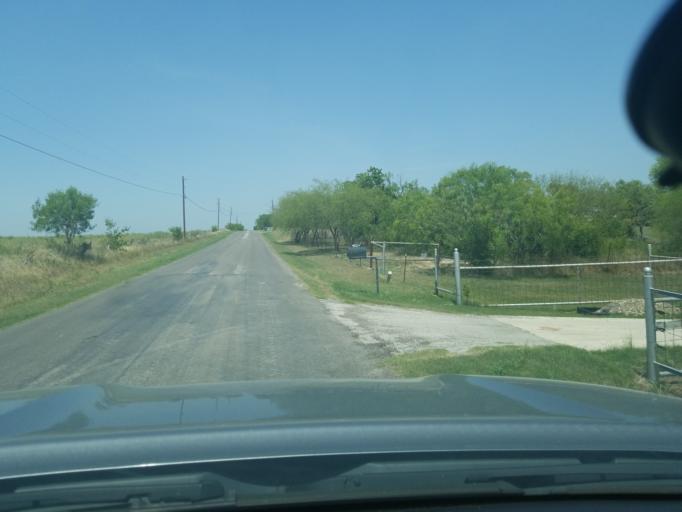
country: US
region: Texas
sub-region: Guadalupe County
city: Cibolo
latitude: 29.5722
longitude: -98.1884
